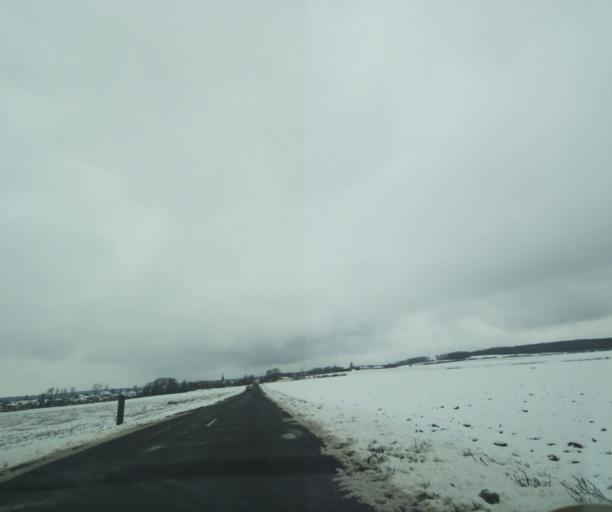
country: FR
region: Champagne-Ardenne
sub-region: Departement de la Haute-Marne
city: Laneuville-a-Remy
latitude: 48.4154
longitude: 4.8289
